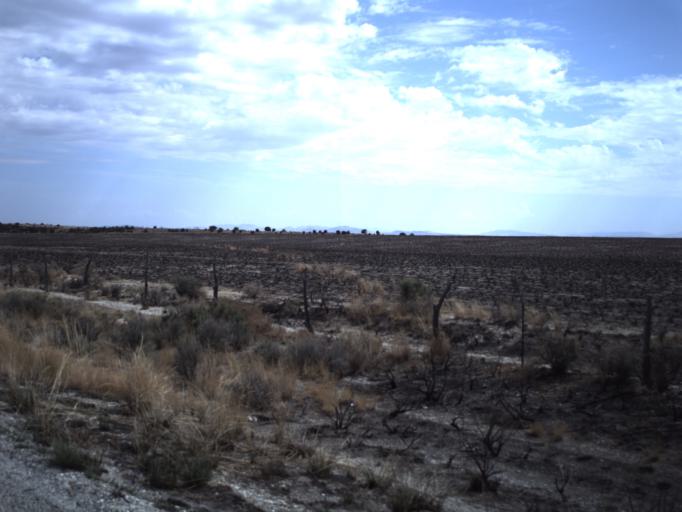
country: US
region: Idaho
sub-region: Minidoka County
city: Rupert
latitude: 41.8286
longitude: -113.1671
